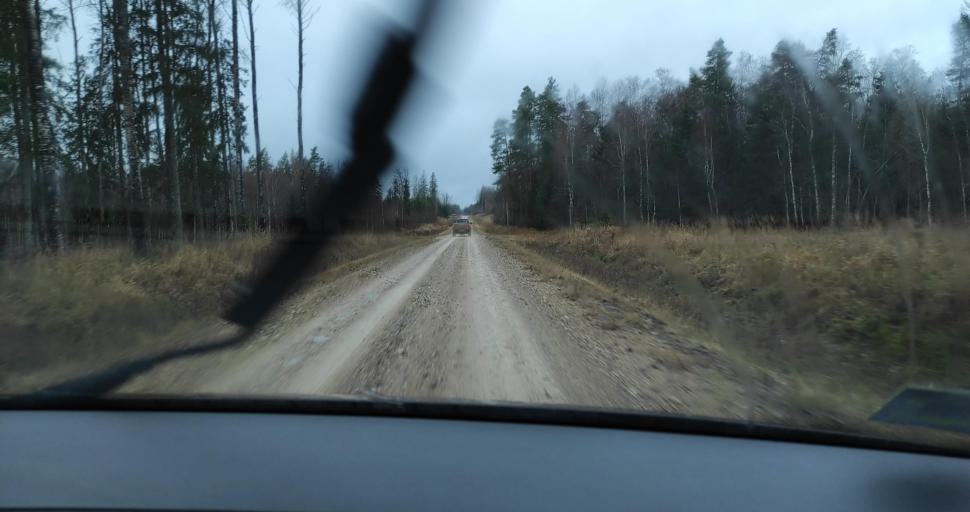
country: LV
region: Skrunda
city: Skrunda
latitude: 56.5600
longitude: 22.0802
